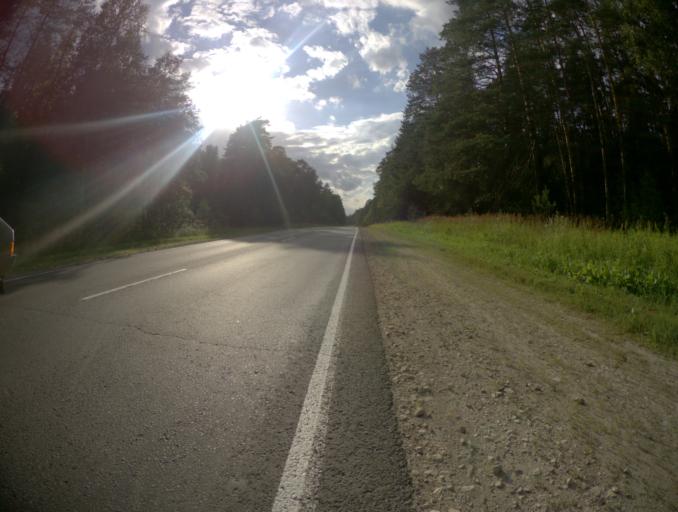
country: RU
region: Vladimir
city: Muromtsevo
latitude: 55.9553
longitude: 40.9982
